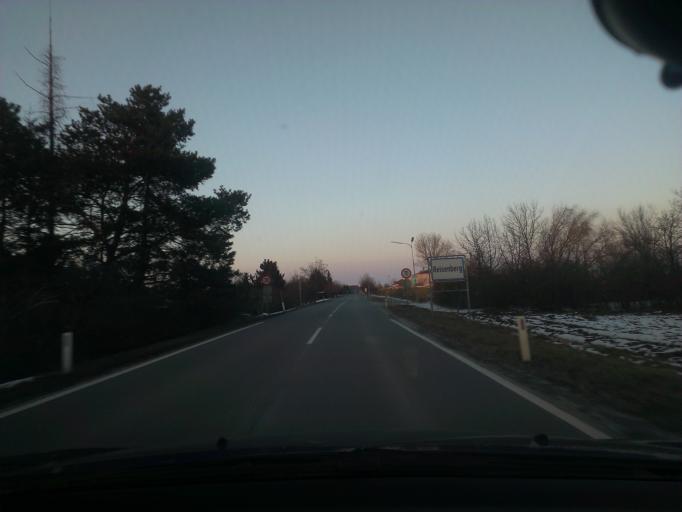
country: AT
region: Lower Austria
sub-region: Politischer Bezirk Baden
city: Reisenberg
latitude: 47.9925
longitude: 16.5209
